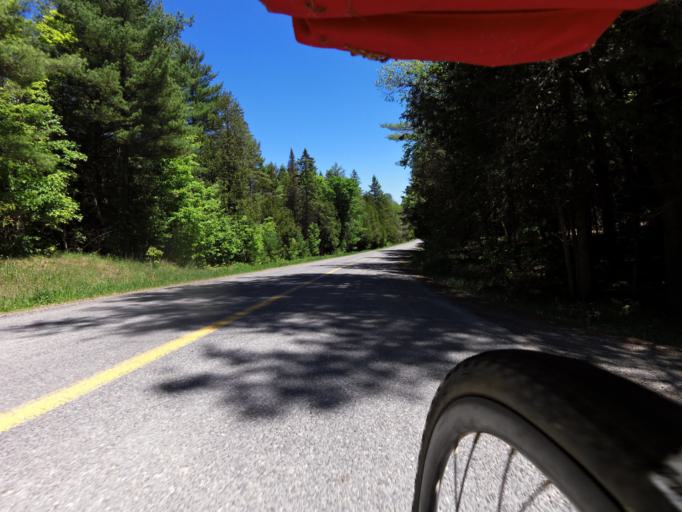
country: CA
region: Ontario
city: Arnprior
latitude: 45.1624
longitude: -76.4441
